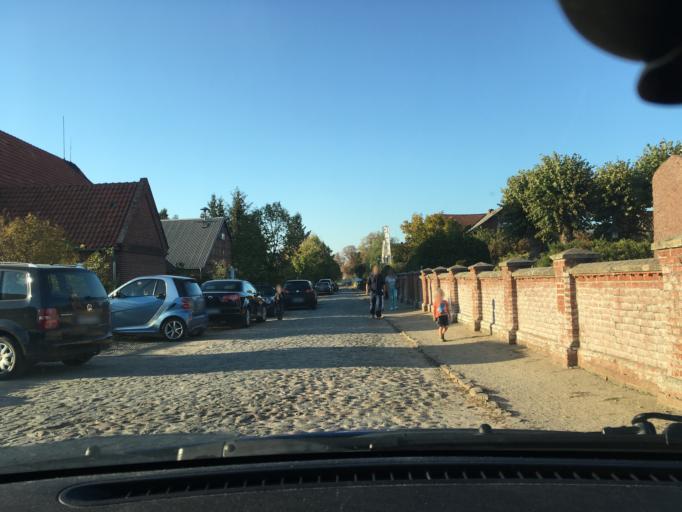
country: DE
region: Lower Saxony
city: Bleckede
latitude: 53.2883
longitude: 10.8015
